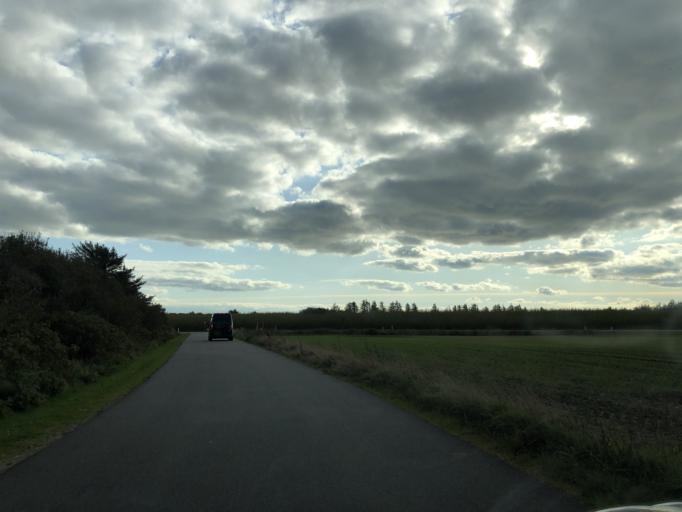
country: DK
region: Central Jutland
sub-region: Holstebro Kommune
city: Ulfborg
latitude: 56.3195
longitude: 8.1575
